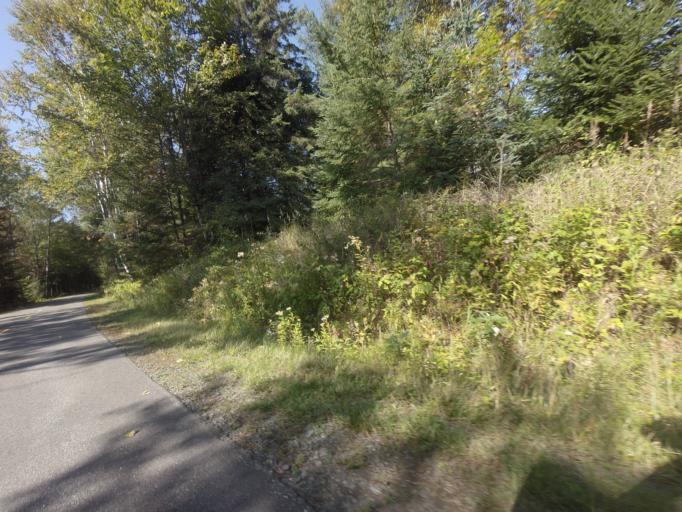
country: CA
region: Quebec
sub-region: Laurentides
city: Mont-Tremblant
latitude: 46.1271
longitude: -74.5721
